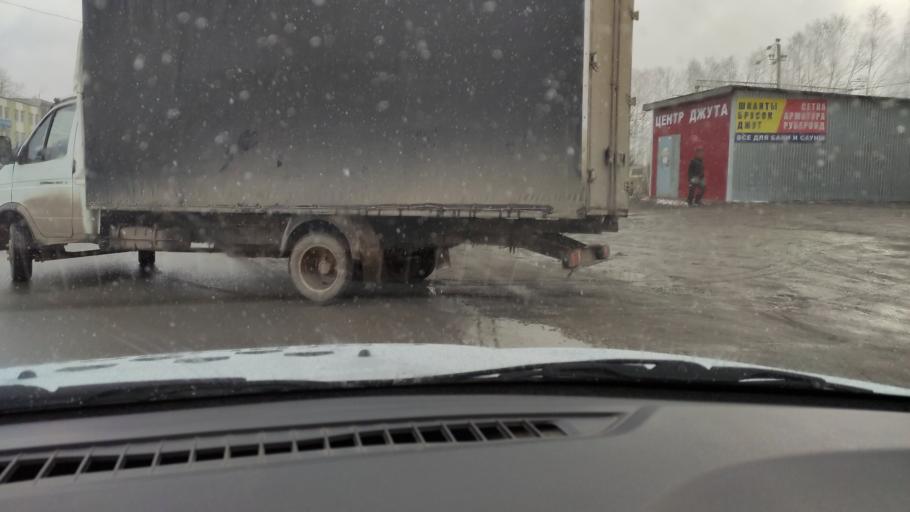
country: RU
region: Perm
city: Perm
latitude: 57.9573
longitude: 56.2130
